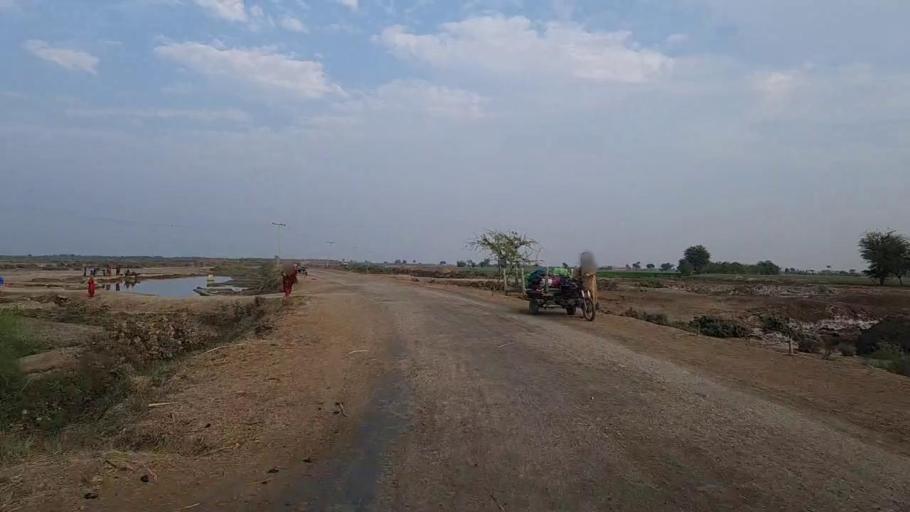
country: PK
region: Sindh
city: Pithoro
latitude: 25.4403
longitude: 69.3015
